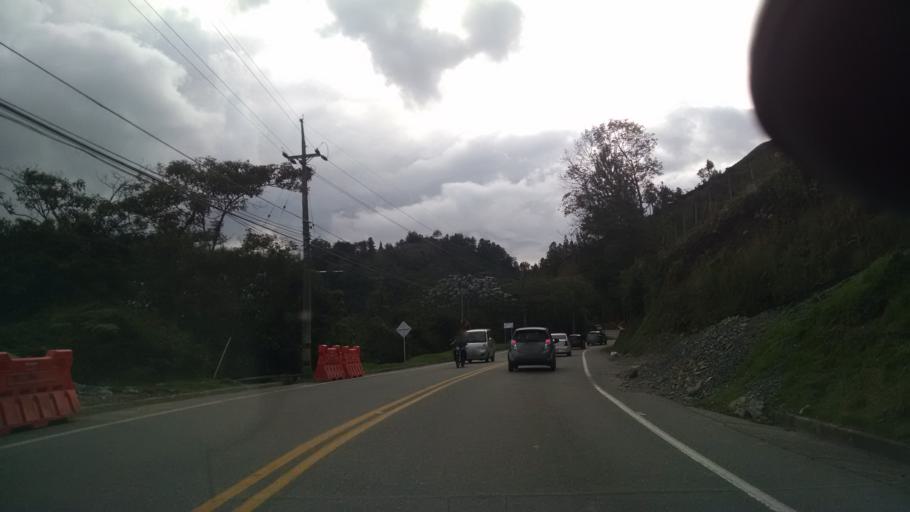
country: CO
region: Antioquia
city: El Retiro
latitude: 6.1395
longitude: -75.5143
